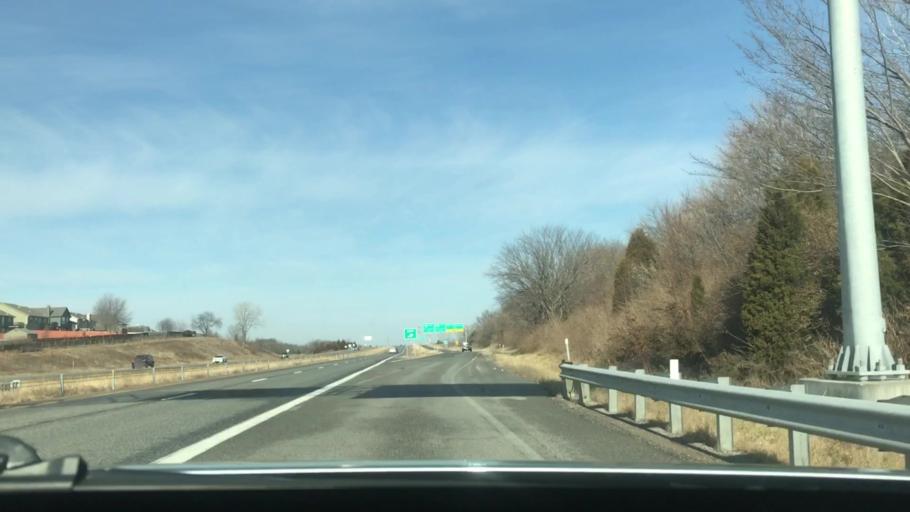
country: US
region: Missouri
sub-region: Clay County
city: Smithville
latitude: 39.2963
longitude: -94.5848
